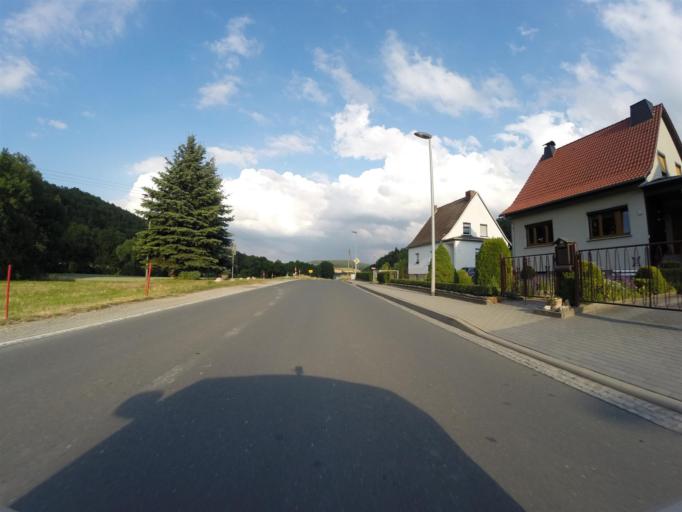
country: DE
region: Thuringia
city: Schops
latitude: 50.8367
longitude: 11.5823
